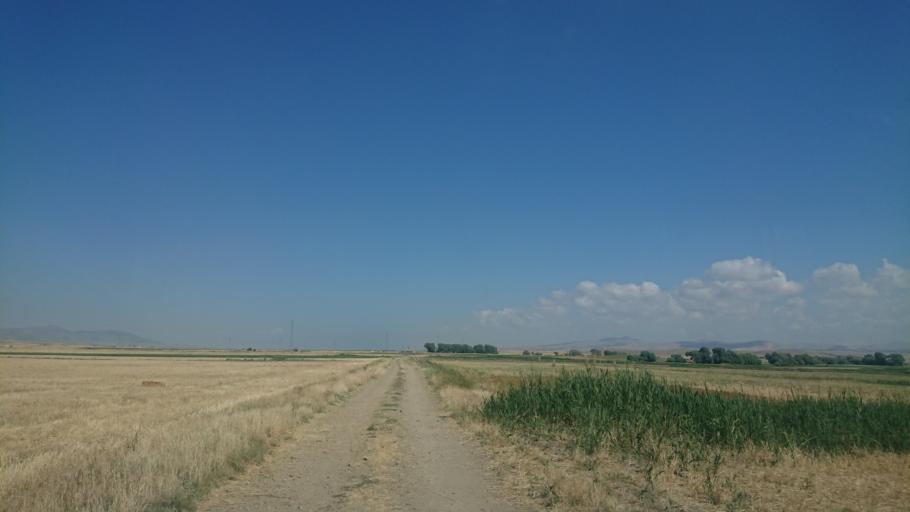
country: TR
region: Aksaray
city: Sariyahsi
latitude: 38.9902
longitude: 33.9003
